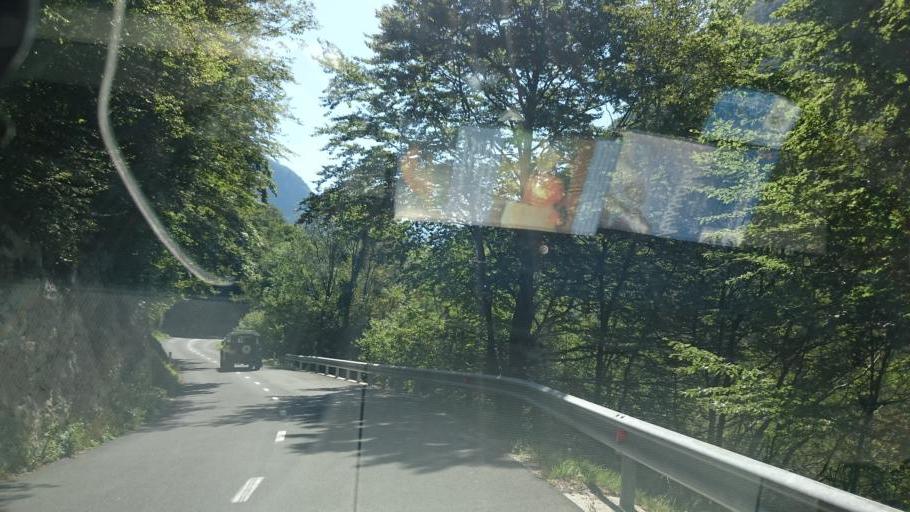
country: SI
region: Bovec
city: Bovec
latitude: 46.3671
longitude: 13.5882
